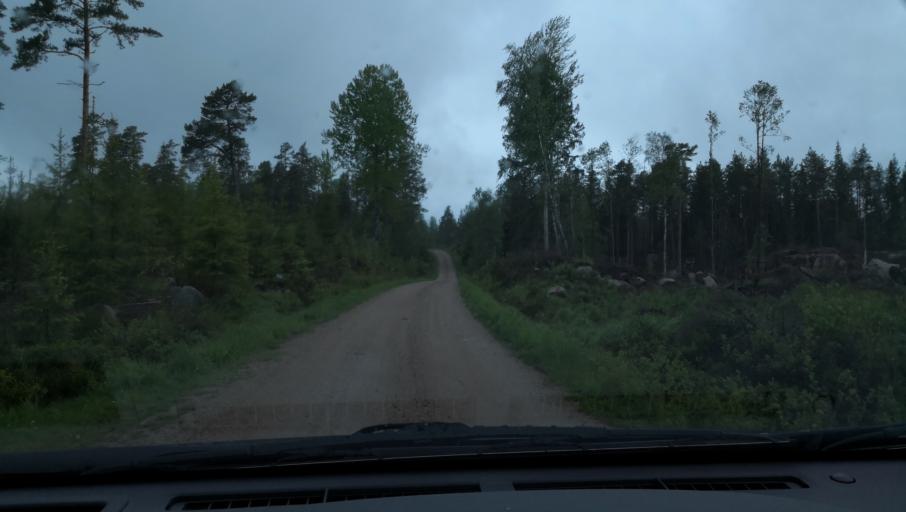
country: SE
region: Uppsala
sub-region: Enkopings Kommun
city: Orsundsbro
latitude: 59.9312
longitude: 17.3288
